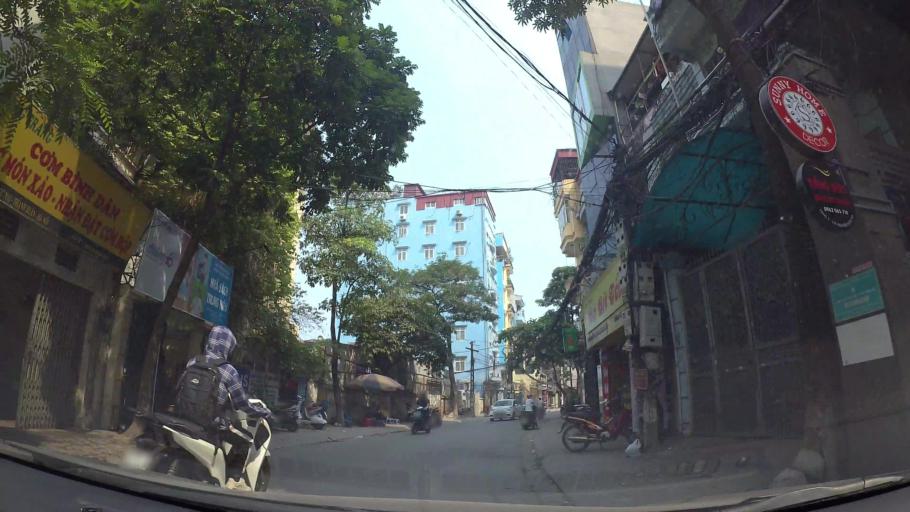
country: VN
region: Ha Noi
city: Dong Da
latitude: 20.9993
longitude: 105.8253
